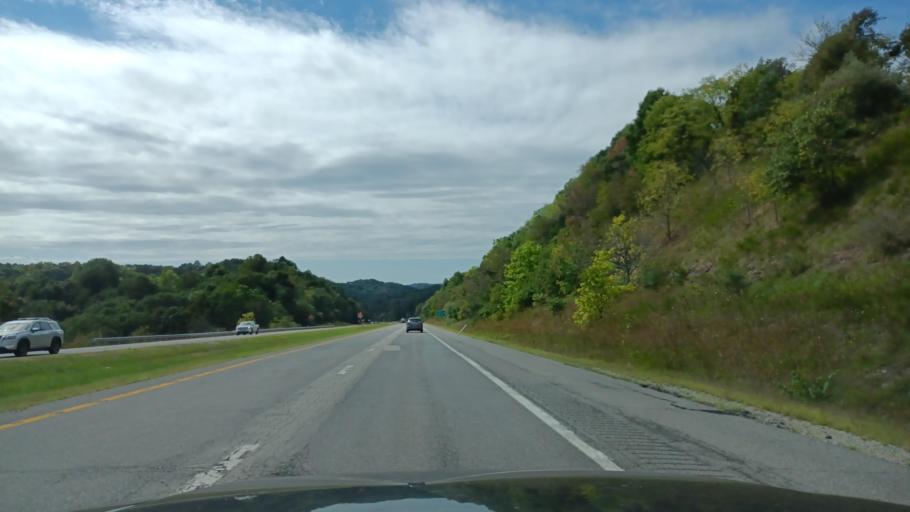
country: US
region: West Virginia
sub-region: Ritchie County
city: Harrisville
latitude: 39.2603
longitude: -81.1624
